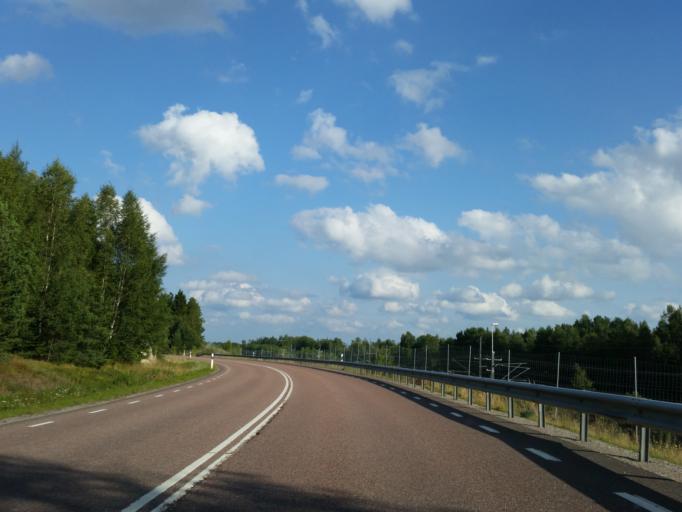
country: SE
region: Stockholm
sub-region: Nykvarns Kommun
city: Nykvarn
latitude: 59.2093
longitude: 17.3375
